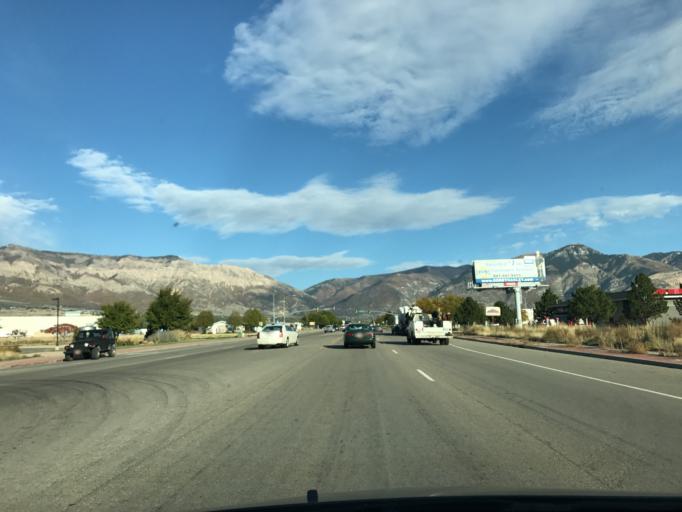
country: US
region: Utah
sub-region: Weber County
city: Farr West
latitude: 41.3067
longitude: -112.0178
